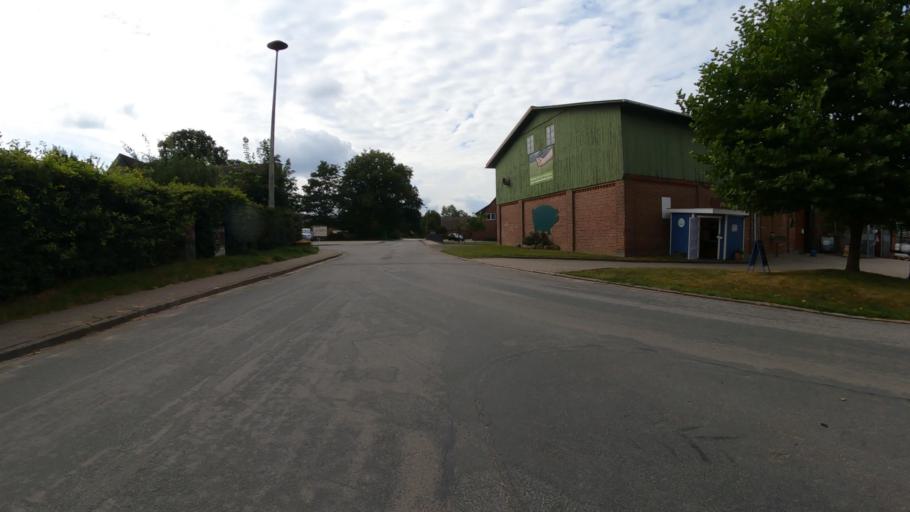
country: DE
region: Lower Saxony
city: Neu Wulmstorf
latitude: 53.4211
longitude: 9.7985
